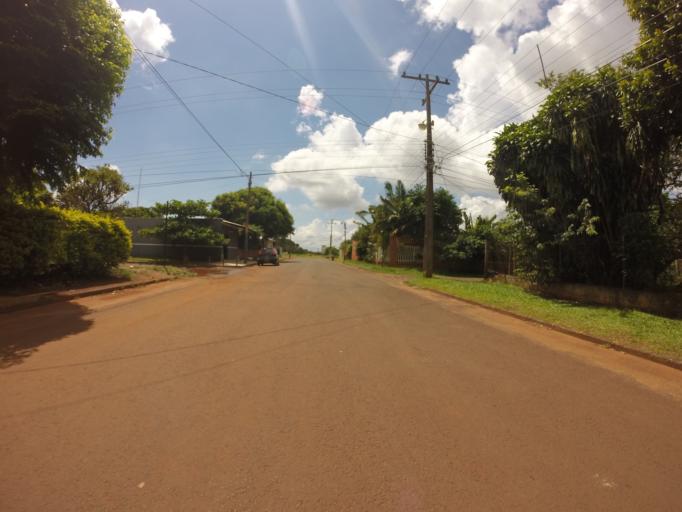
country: PY
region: Alto Parana
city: Ciudad del Este
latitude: -25.4073
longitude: -54.6229
